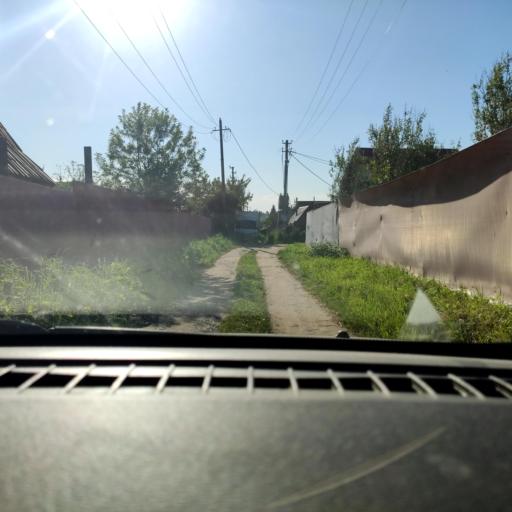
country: RU
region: Perm
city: Overyata
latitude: 58.1166
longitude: 55.8829
